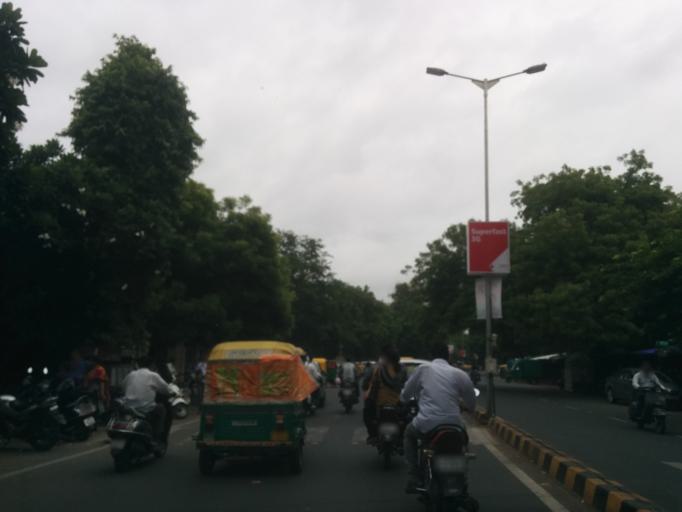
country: IN
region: Gujarat
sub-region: Ahmadabad
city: Ahmedabad
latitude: 23.0252
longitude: 72.5594
